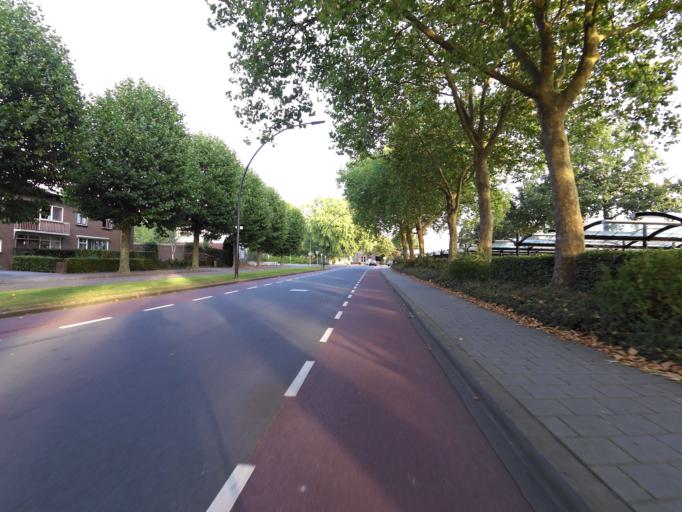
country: NL
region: Gelderland
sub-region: Gemeente Zevenaar
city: Zevenaar
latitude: 51.9236
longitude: 6.0716
